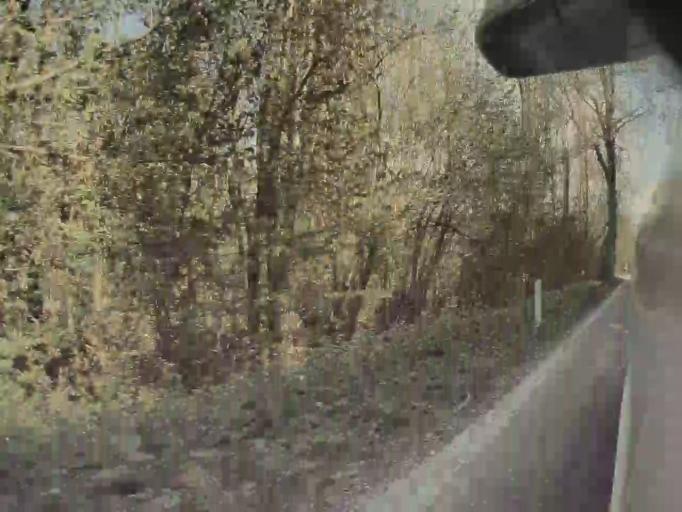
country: BE
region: Wallonia
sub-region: Province du Luxembourg
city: Tellin
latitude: 50.0296
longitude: 5.2066
